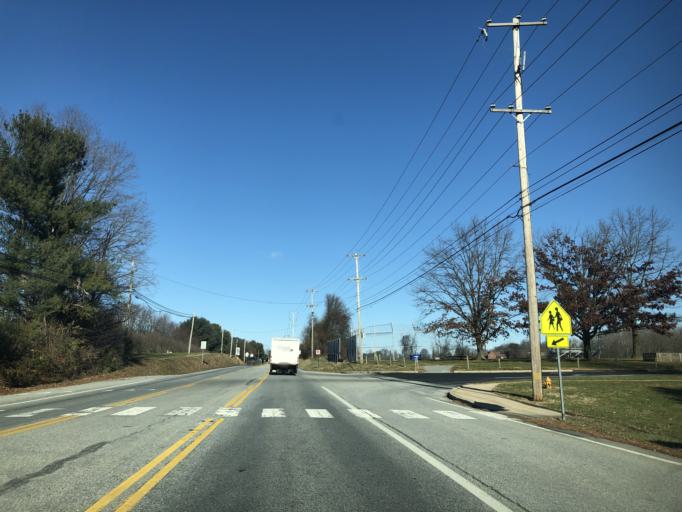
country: US
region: Pennsylvania
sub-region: Chester County
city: Kennett Square
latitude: 39.8860
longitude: -75.7216
